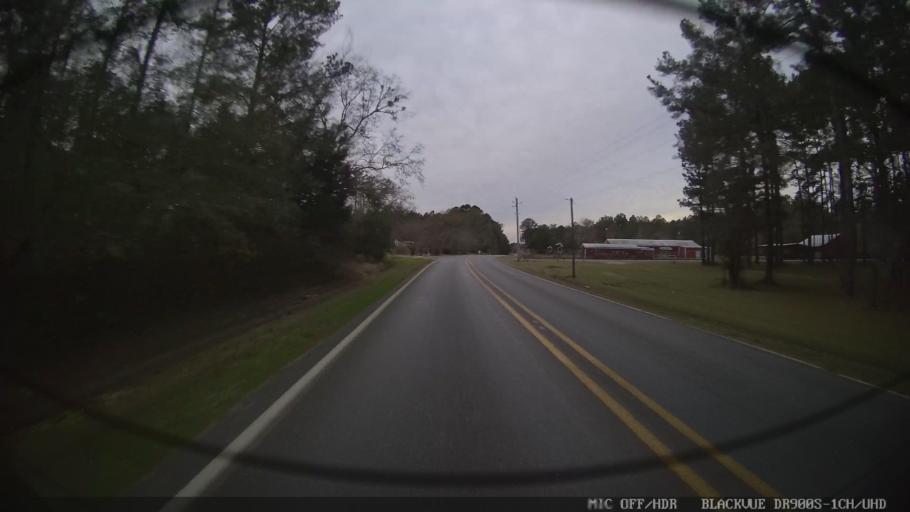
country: US
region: Mississippi
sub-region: Clarke County
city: Quitman
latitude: 32.0292
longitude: -88.7967
